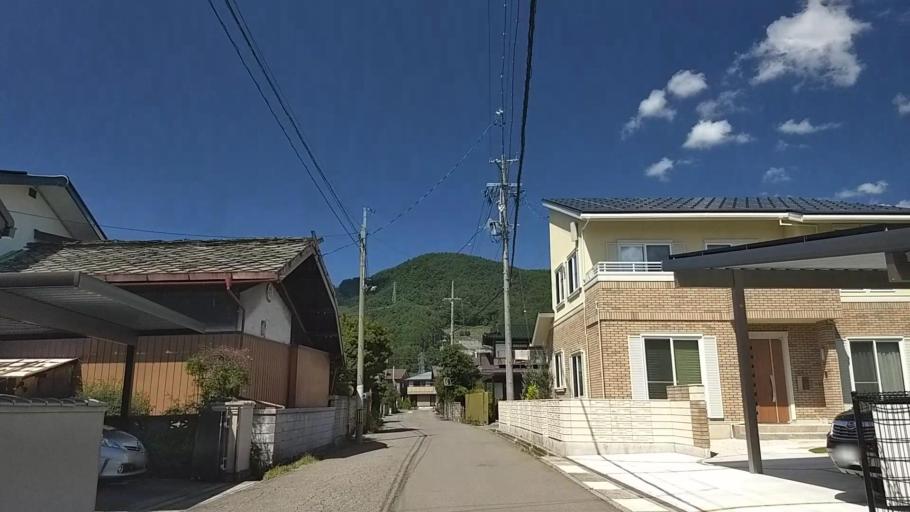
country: JP
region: Nagano
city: Chino
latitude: 35.9955
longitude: 138.1551
